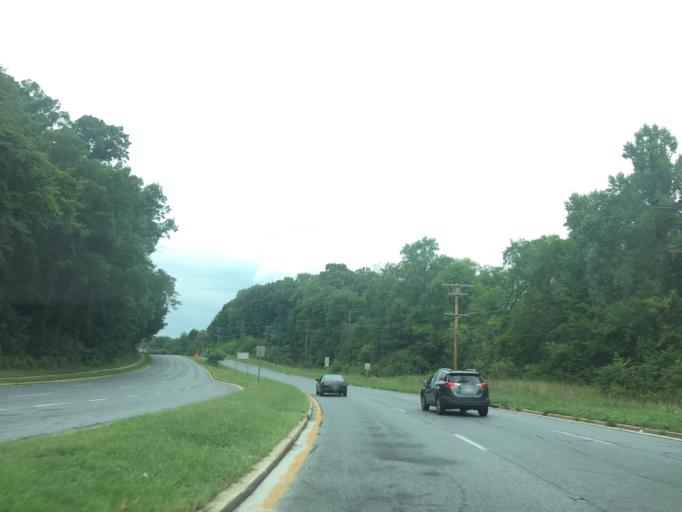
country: US
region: Maryland
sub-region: Baltimore County
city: Woodlawn
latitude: 39.3110
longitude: -76.7170
